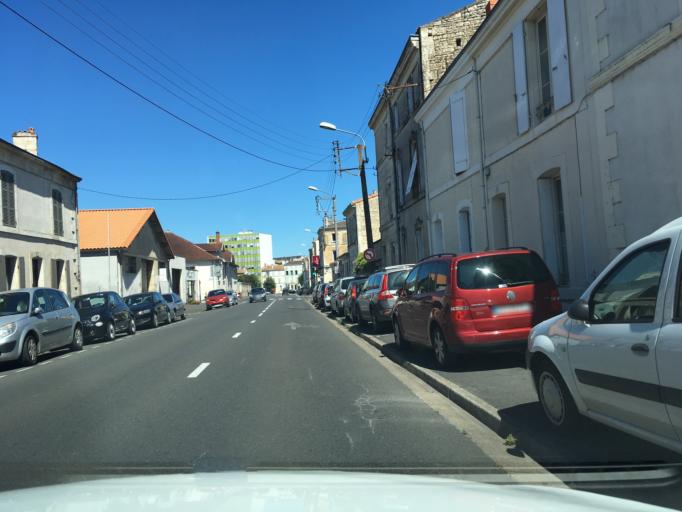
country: FR
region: Poitou-Charentes
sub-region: Departement des Deux-Sevres
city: Niort
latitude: 46.3232
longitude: -0.4529
